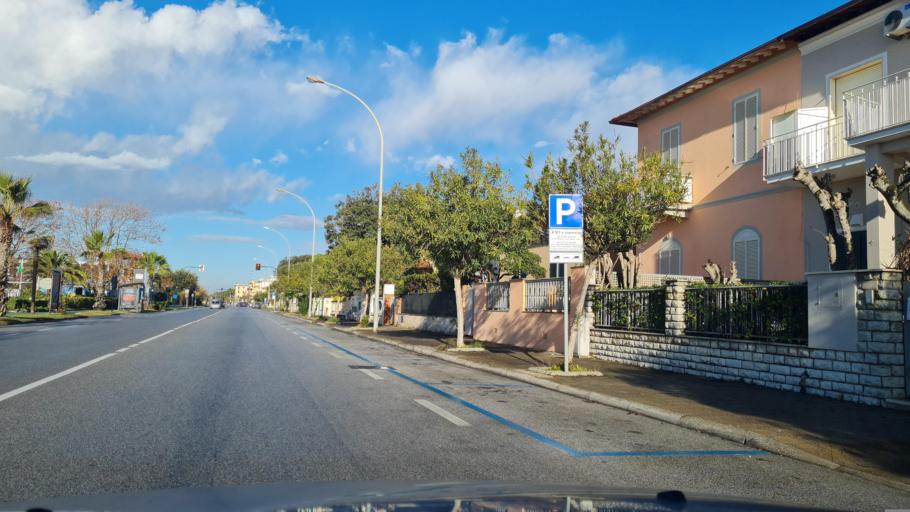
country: IT
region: Tuscany
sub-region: Provincia di Lucca
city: Pietrasanta
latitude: 43.9348
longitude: 10.1921
